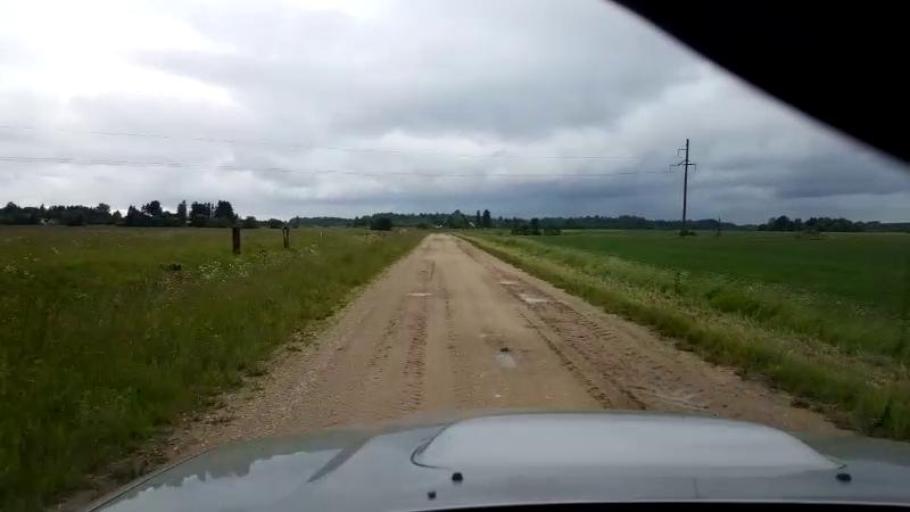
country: EE
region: Paernumaa
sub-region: Halinga vald
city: Parnu-Jaagupi
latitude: 58.5339
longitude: 24.5689
